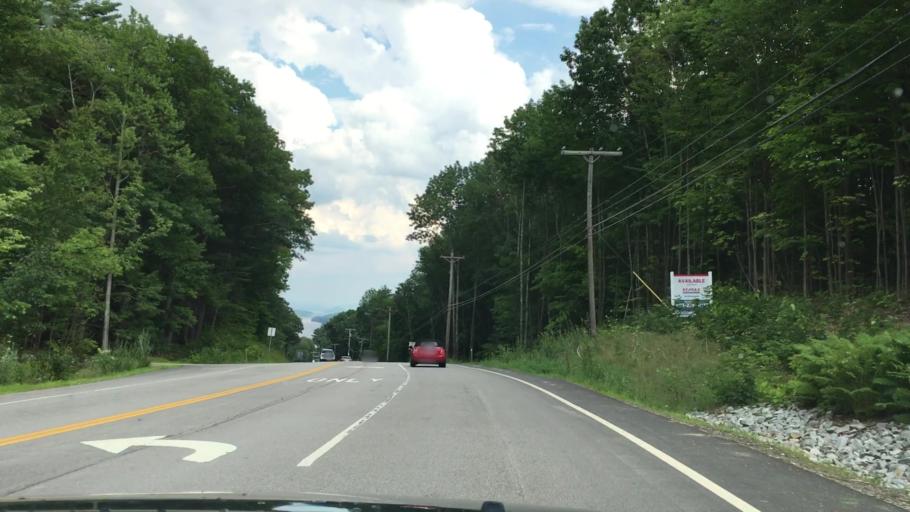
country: US
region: New Hampshire
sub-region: Belknap County
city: Meredith
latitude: 43.6385
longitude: -71.4972
